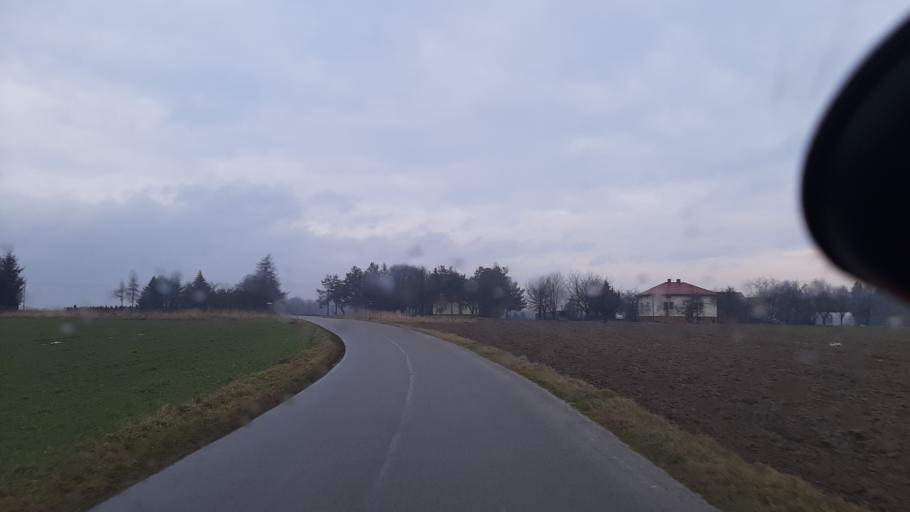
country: PL
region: Lublin Voivodeship
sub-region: Powiat lubelski
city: Niemce
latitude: 51.3338
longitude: 22.5869
